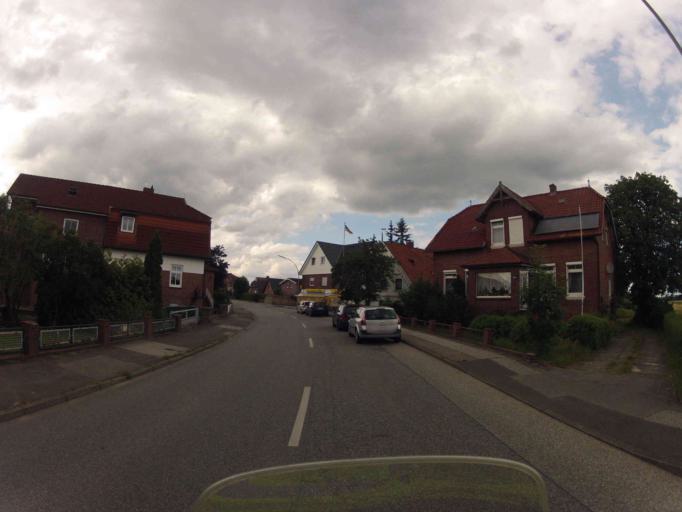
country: DE
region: Lower Saxony
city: Stelle
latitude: 53.4191
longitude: 10.1502
